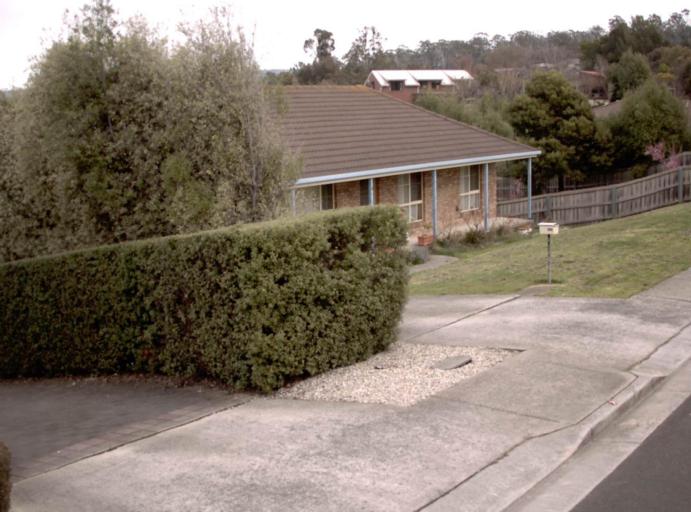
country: AU
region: Tasmania
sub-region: Launceston
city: Newstead
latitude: -41.4641
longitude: 147.1798
